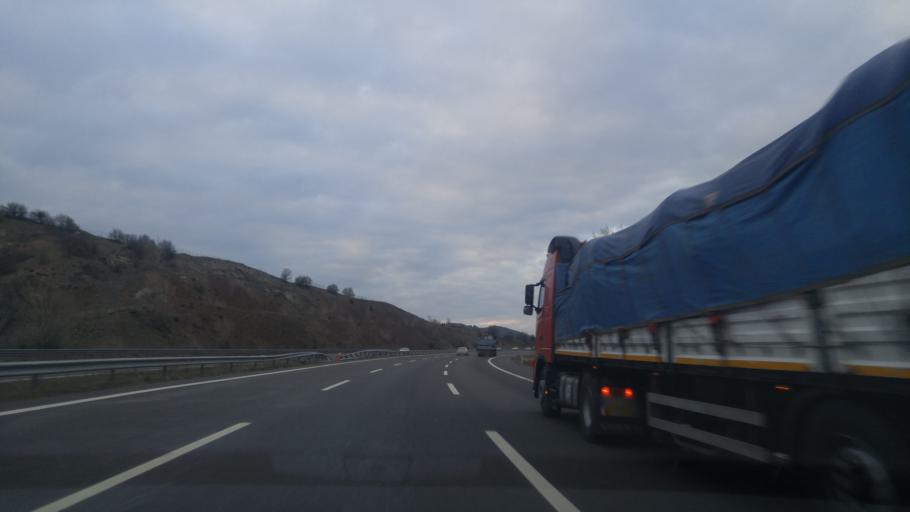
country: TR
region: Ankara
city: Celtikci
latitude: 40.3514
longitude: 32.4712
